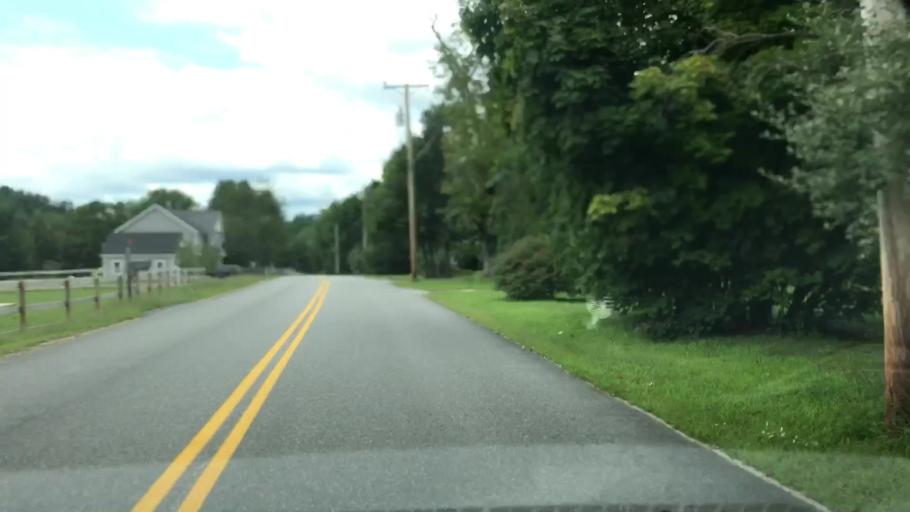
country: US
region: New Hampshire
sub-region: Hillsborough County
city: Milford
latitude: 42.8221
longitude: -71.5952
